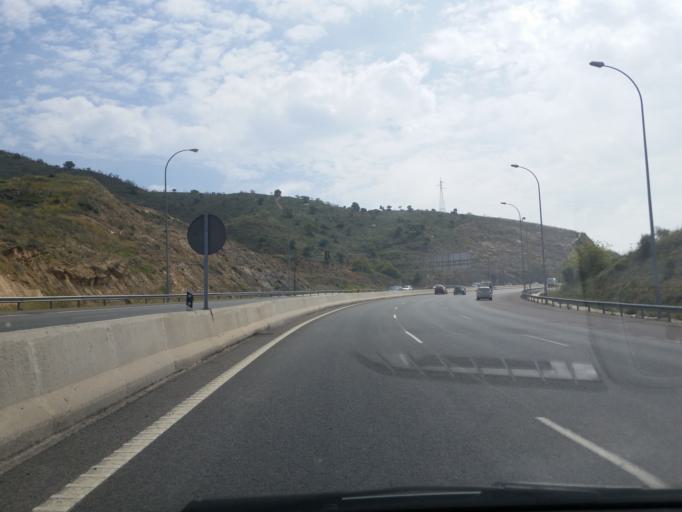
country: ES
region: Andalusia
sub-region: Provincia de Malaga
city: Malaga
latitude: 36.7561
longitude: -4.4179
